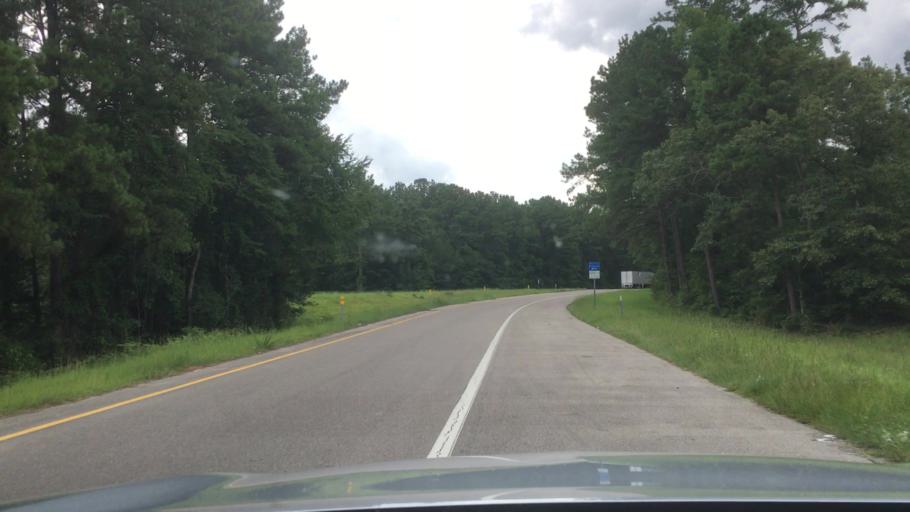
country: US
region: Mississippi
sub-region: Clarke County
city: Stonewall
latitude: 32.1652
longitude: -88.8662
